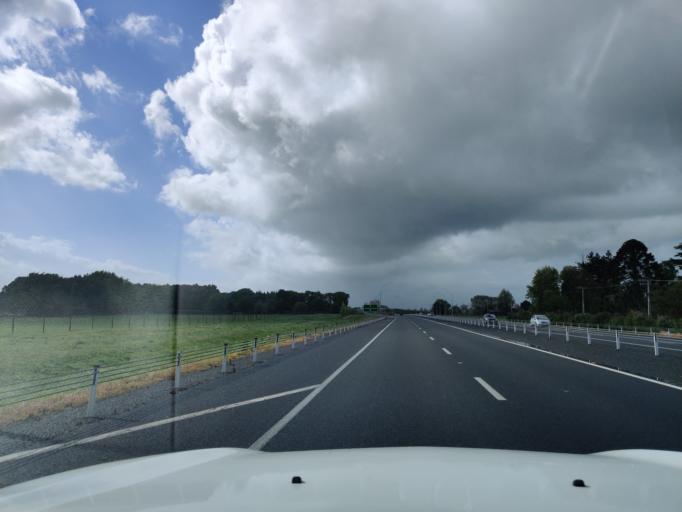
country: NZ
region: Waikato
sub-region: Waipa District
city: Cambridge
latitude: -37.8608
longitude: 175.3986
